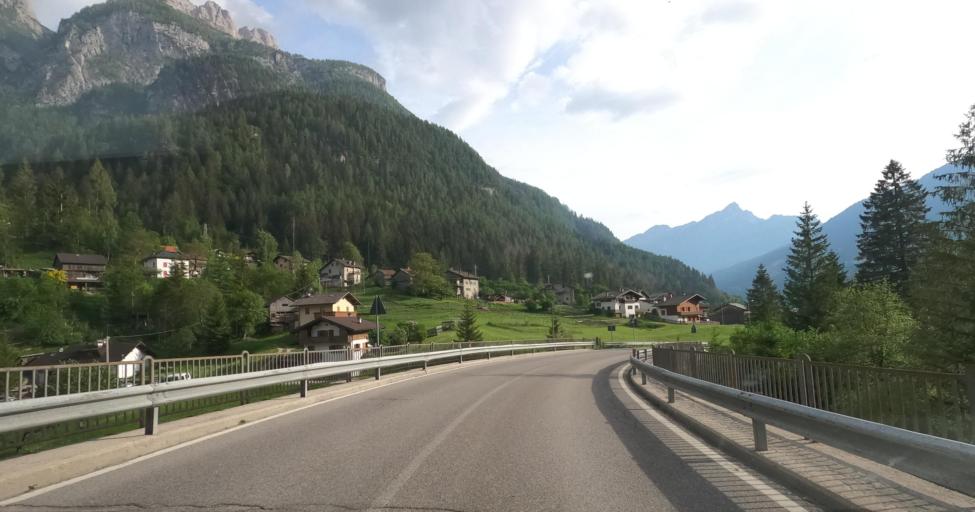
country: IT
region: Veneto
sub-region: Provincia di Belluno
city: Celat-San Tomaso Agordino
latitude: 46.3879
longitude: 11.9988
